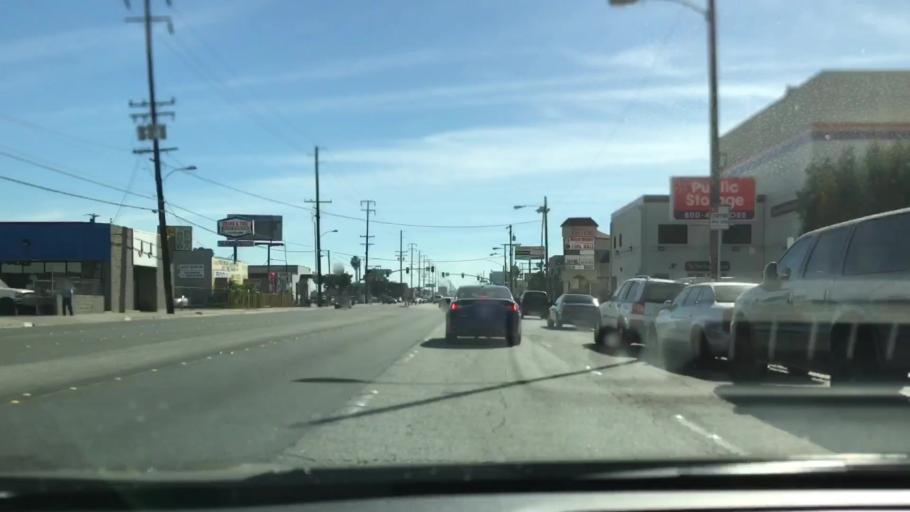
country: US
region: California
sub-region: Los Angeles County
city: Alondra Park
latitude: 33.9037
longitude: -118.3266
